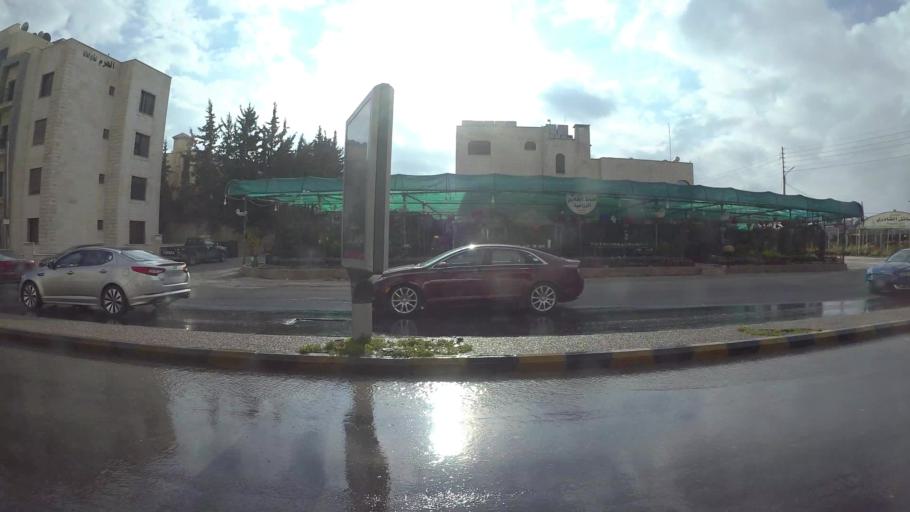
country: JO
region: Amman
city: Wadi as Sir
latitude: 31.9825
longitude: 35.8386
